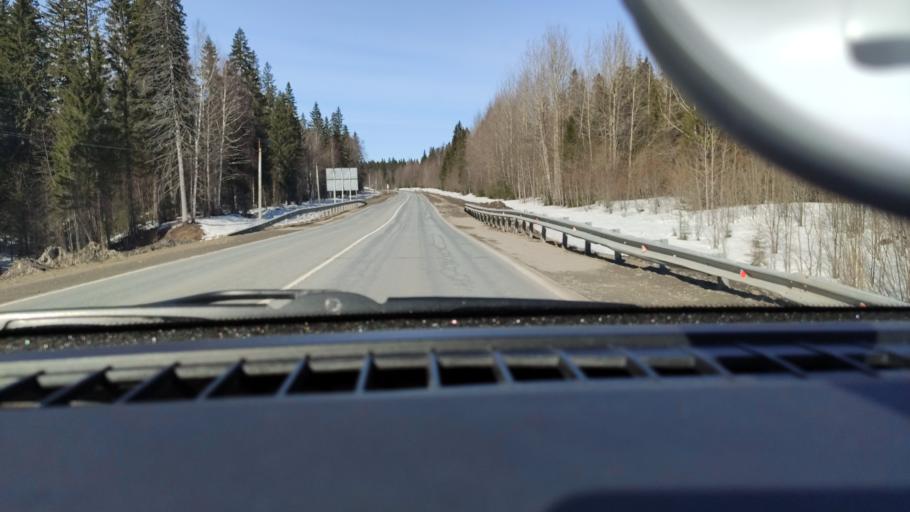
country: RU
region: Perm
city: Perm
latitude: 58.1976
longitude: 56.2086
